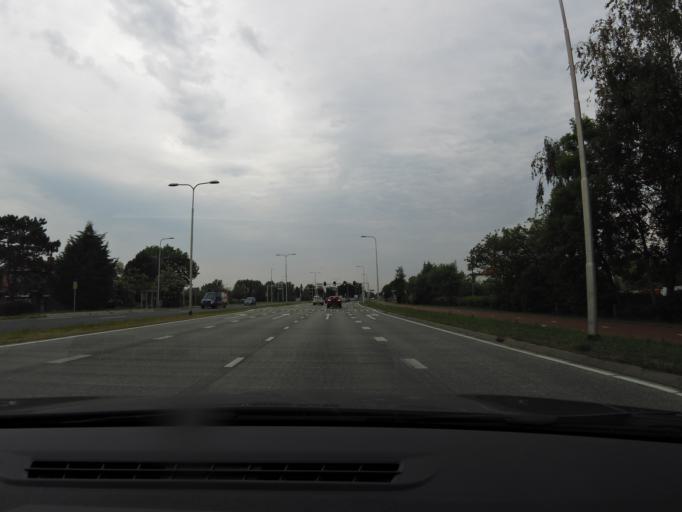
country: NL
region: South Holland
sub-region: Gemeente Albrandswaard
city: Rhoon
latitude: 51.8580
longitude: 4.4106
